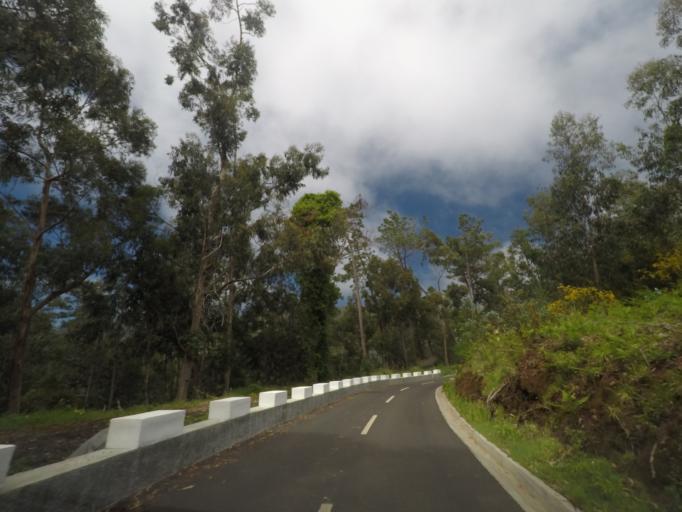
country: PT
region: Madeira
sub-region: Calheta
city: Arco da Calheta
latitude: 32.7212
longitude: -17.1238
